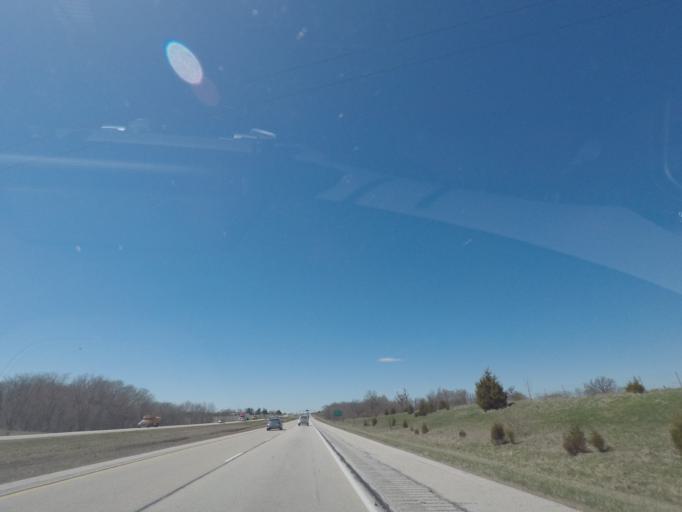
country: US
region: Illinois
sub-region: McLean County
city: Hudson
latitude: 40.5839
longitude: -88.8797
